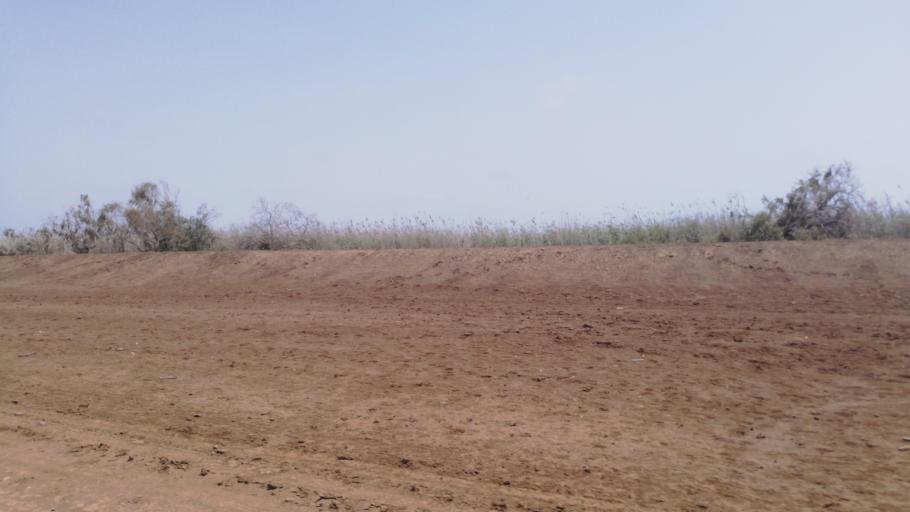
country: SN
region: Saint-Louis
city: Saint-Louis
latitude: 16.4016
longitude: -16.2910
